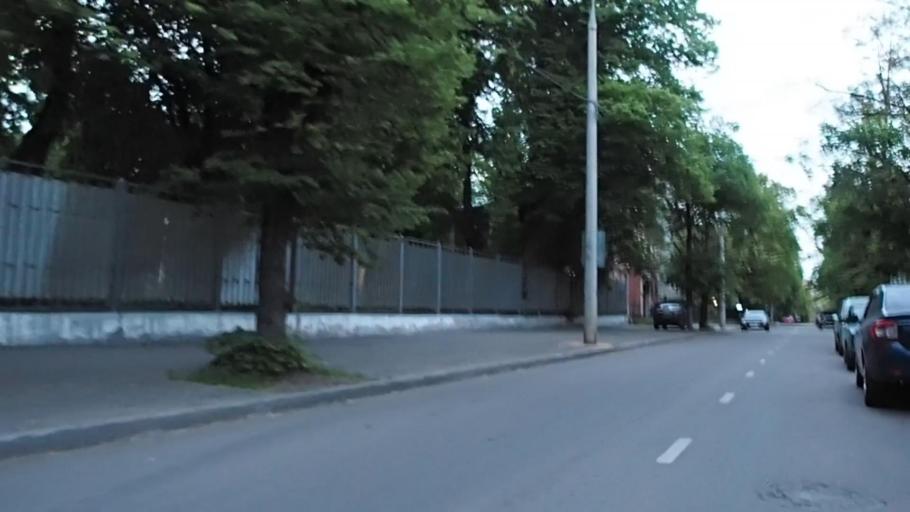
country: RU
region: Moscow
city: Sokol'niki
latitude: 55.7910
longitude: 37.6911
